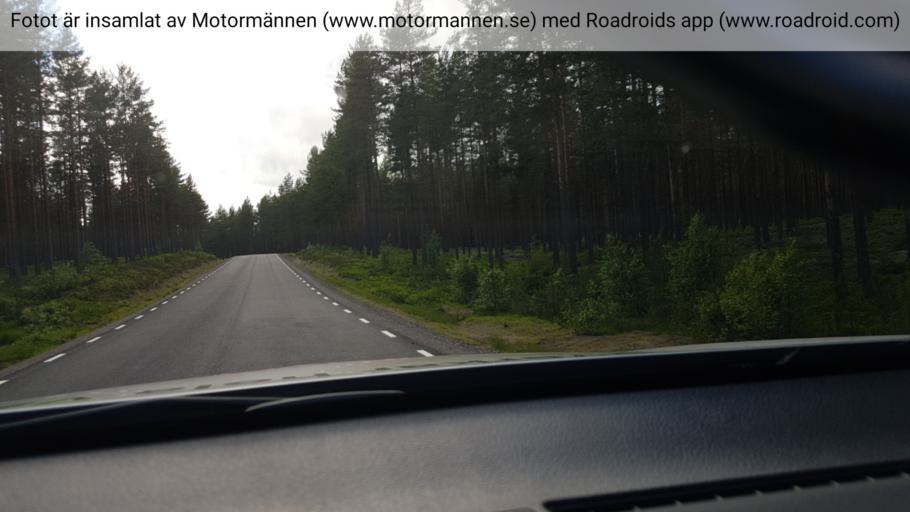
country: SE
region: Vaermland
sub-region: Hagfors Kommun
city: Ekshaerad
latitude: 60.2970
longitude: 13.4219
